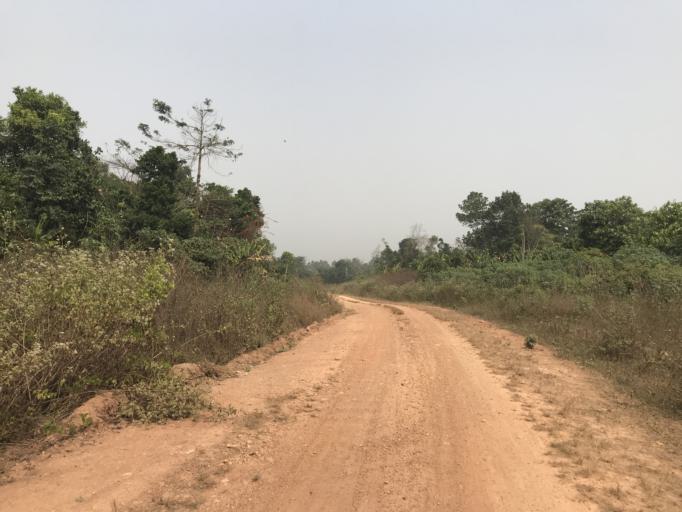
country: NG
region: Osun
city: Ifetedo
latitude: 7.0491
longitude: 4.4712
